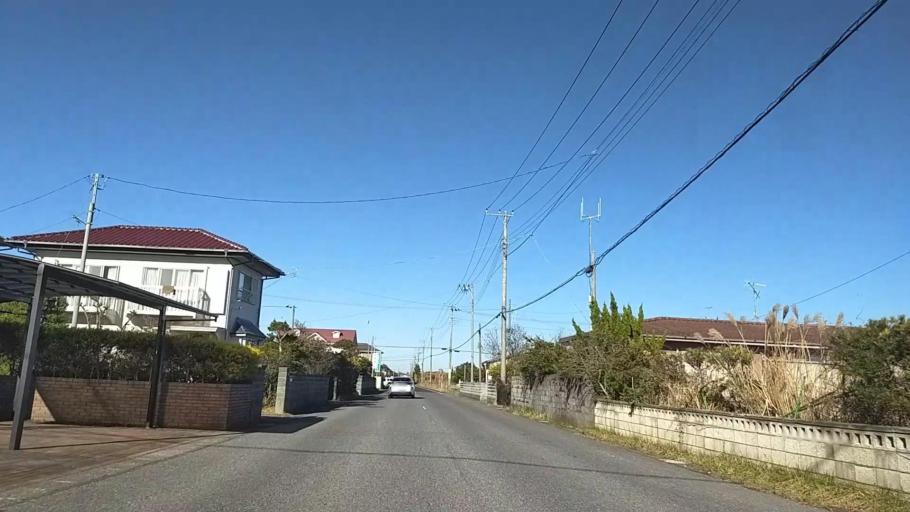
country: JP
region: Chiba
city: Mobara
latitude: 35.4078
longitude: 140.3881
